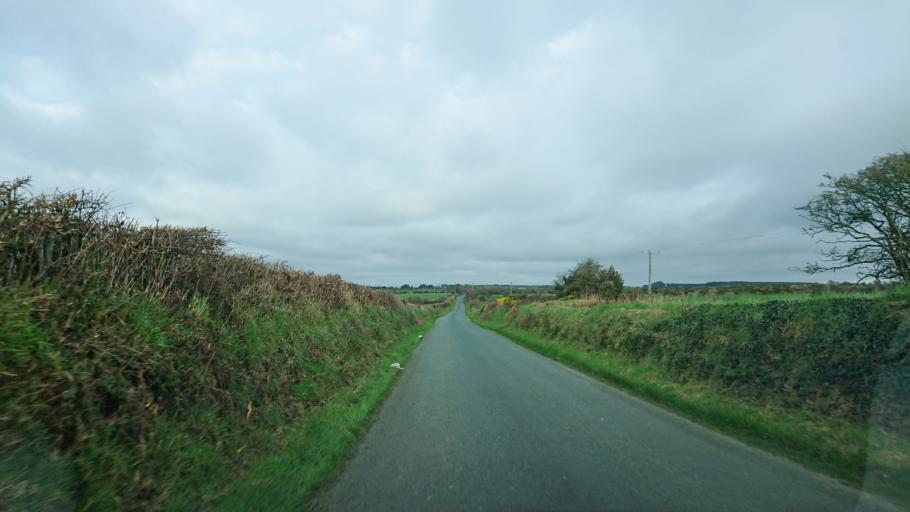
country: IE
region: Munster
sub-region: Waterford
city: Portlaw
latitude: 52.1534
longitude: -7.3095
